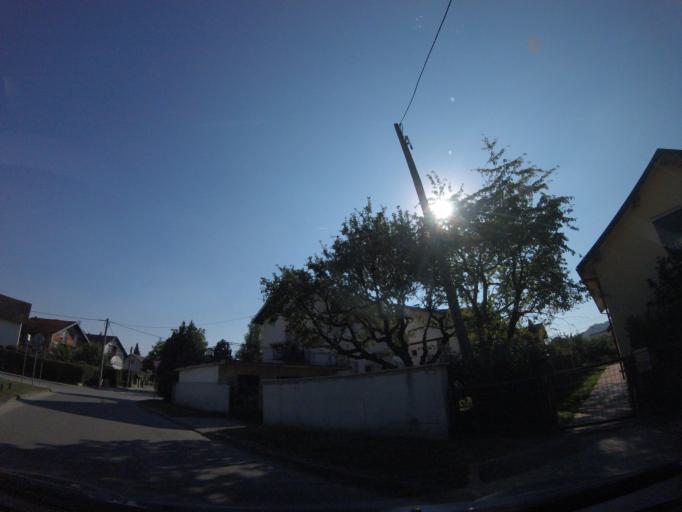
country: HR
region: Zagrebacka
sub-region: Grad Samobor
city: Samobor
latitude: 45.8060
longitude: 15.7299
